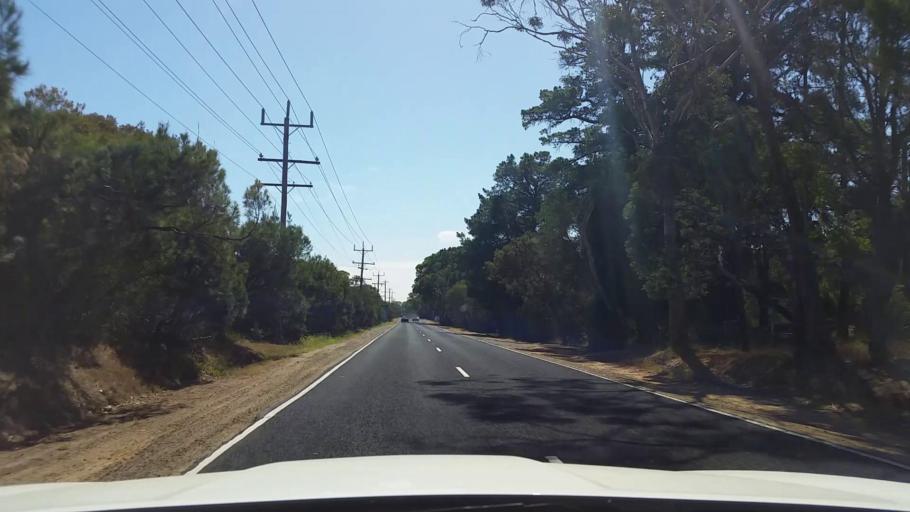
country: AU
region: Victoria
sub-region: Mornington Peninsula
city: Somerville
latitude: -38.2106
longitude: 145.1573
